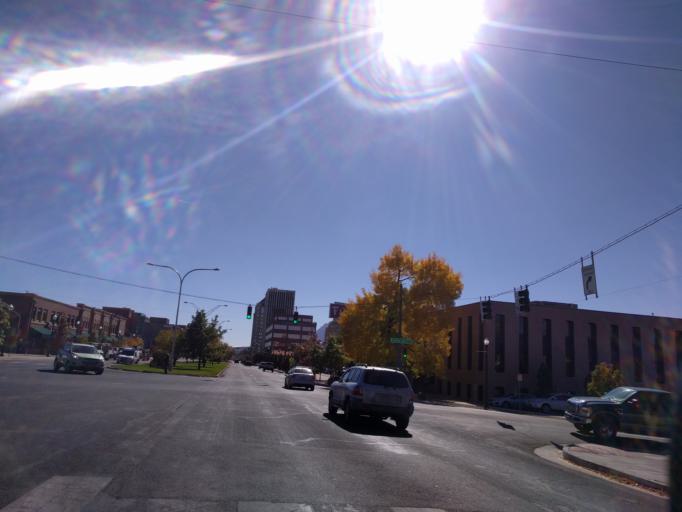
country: US
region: Colorado
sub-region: El Paso County
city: Colorado Springs
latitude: 38.8384
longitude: -104.8253
